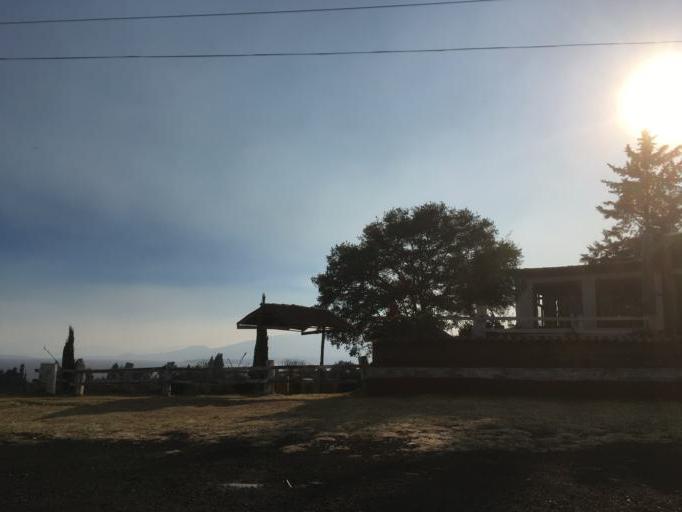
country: MX
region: Michoacan
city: Santa Fe de la Laguna
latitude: 19.6814
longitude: -101.5770
